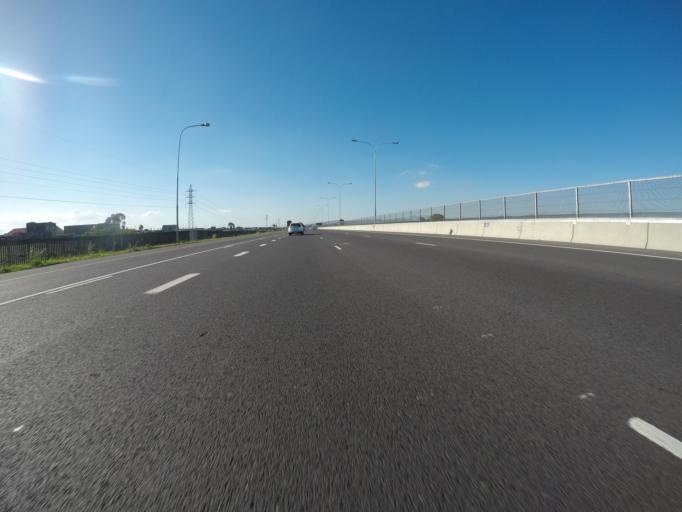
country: ZA
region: Western Cape
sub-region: City of Cape Town
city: Lansdowne
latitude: -33.9942
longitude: 18.6403
